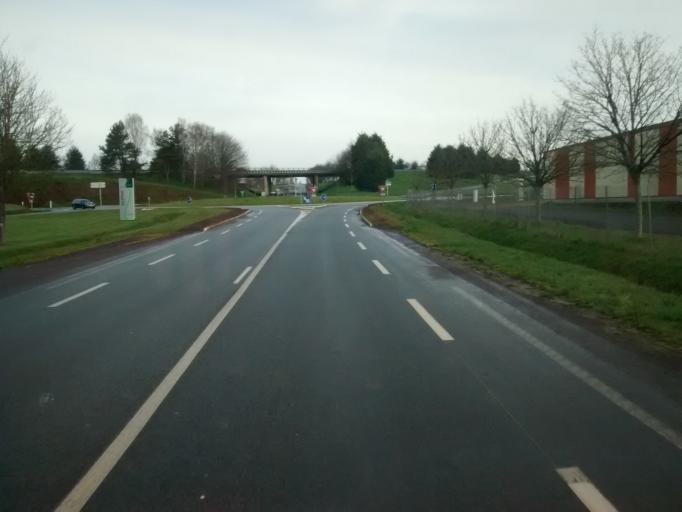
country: FR
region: Brittany
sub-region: Departement du Morbihan
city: Malestroit
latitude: 47.8496
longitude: -2.4187
